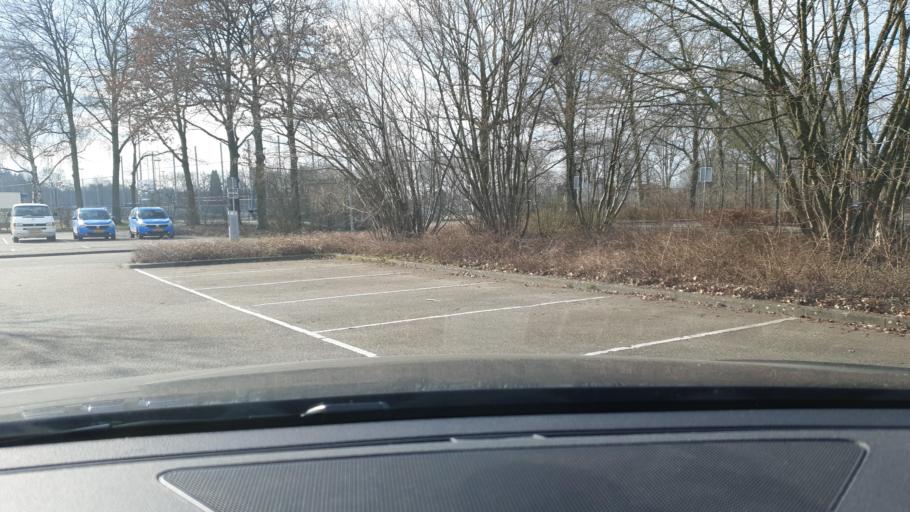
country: NL
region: North Brabant
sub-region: Gemeente Veldhoven
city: Veldhoven
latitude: 51.4004
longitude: 5.3875
